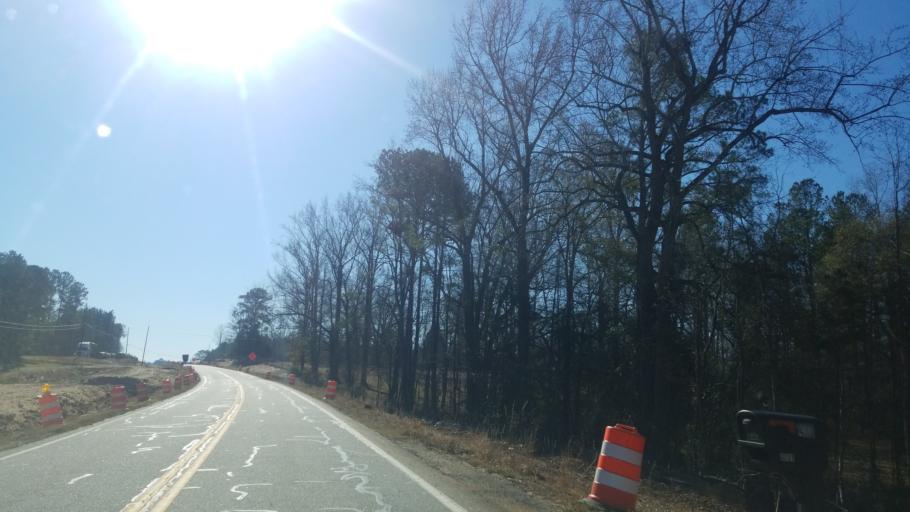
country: US
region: Alabama
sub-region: Lee County
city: Smiths Station
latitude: 32.6594
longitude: -85.0599
